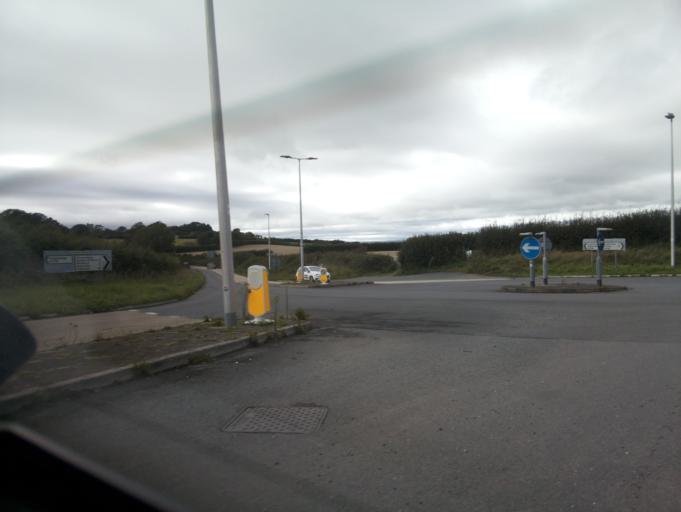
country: GB
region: England
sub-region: Devon
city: Kingsbridge
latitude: 50.2973
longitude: -3.7978
